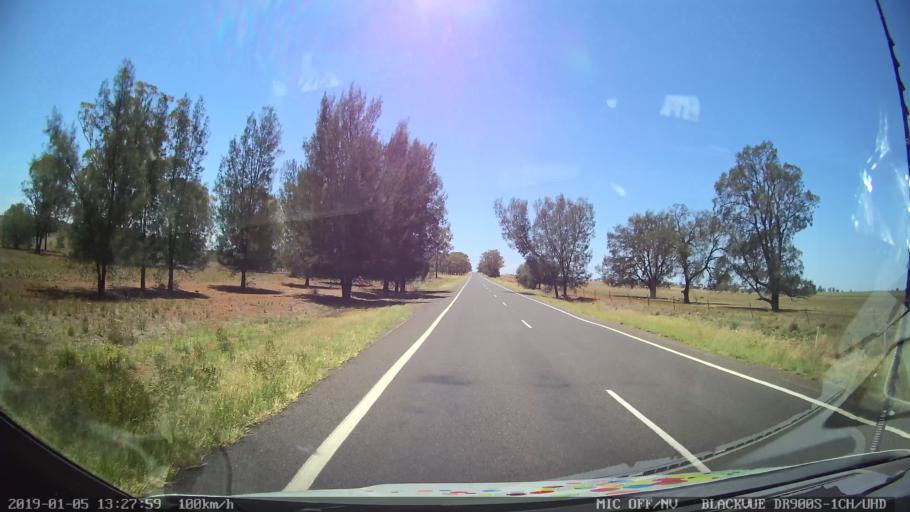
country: AU
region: New South Wales
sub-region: Gunnedah
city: Gunnedah
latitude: -31.0397
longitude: 150.0371
